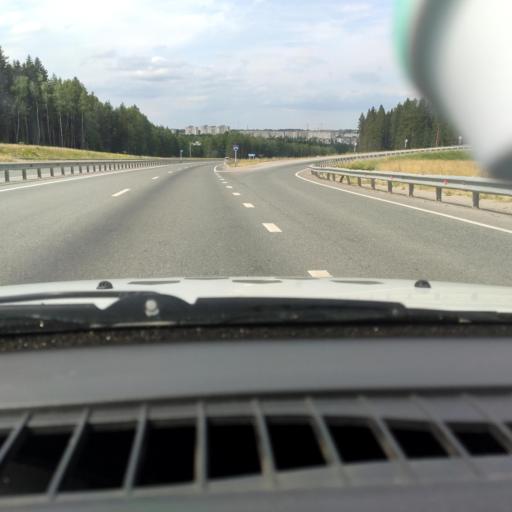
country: RU
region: Perm
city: Berezniki
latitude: 59.4054
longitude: 56.8816
